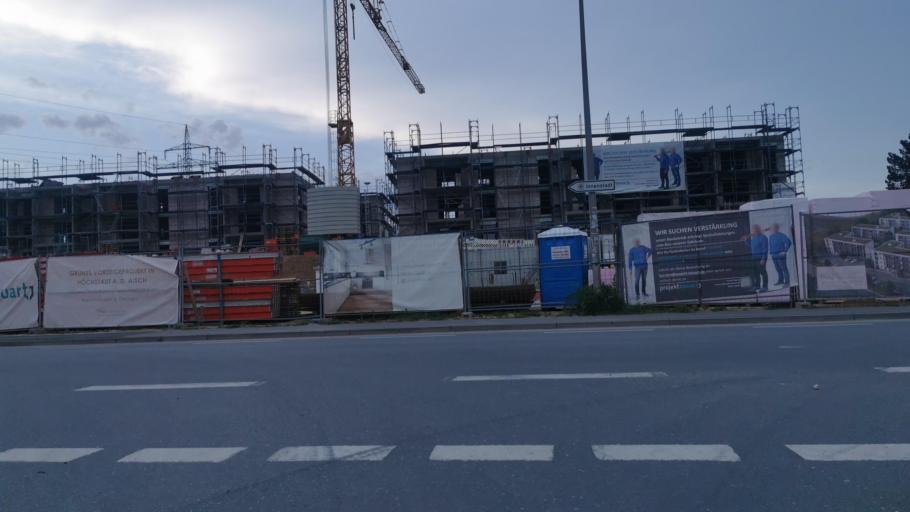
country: DE
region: Bavaria
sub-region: Regierungsbezirk Mittelfranken
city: Hochstadt an der Aisch
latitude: 49.7074
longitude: 10.8267
